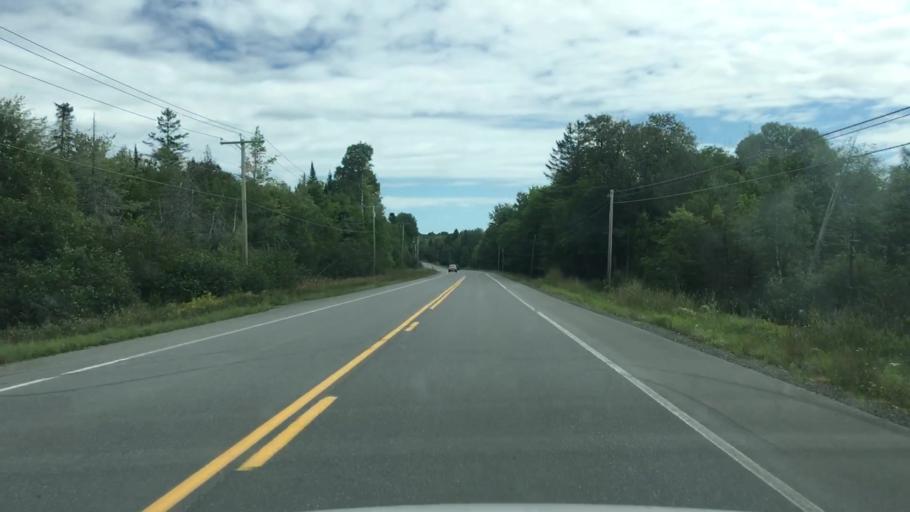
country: US
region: Maine
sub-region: Piscataquis County
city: Milo
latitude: 45.2417
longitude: -69.0341
